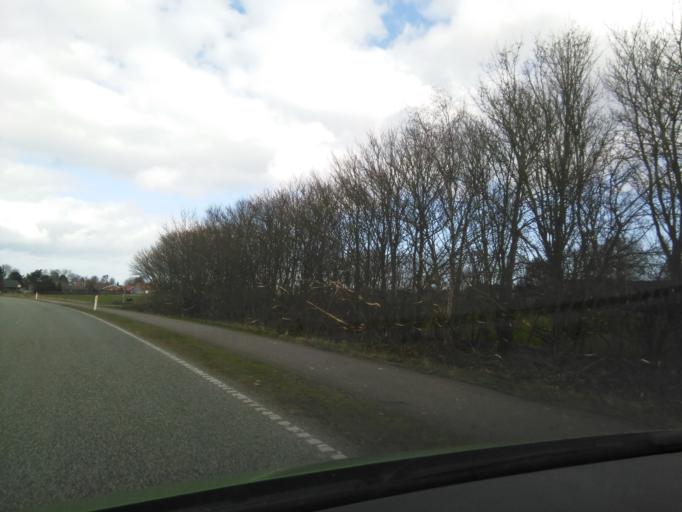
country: DK
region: Central Jutland
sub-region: Arhus Kommune
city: Beder
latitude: 56.0166
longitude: 10.2619
